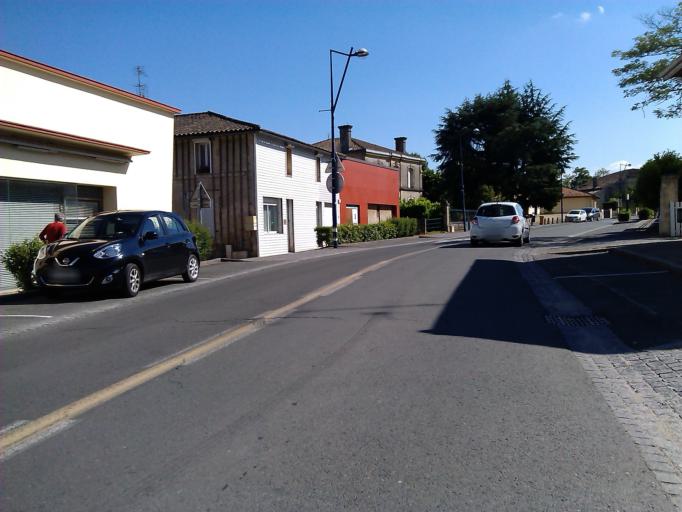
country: FR
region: Aquitaine
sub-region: Departement de la Gironde
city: Cavignac
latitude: 45.1032
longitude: -0.3877
